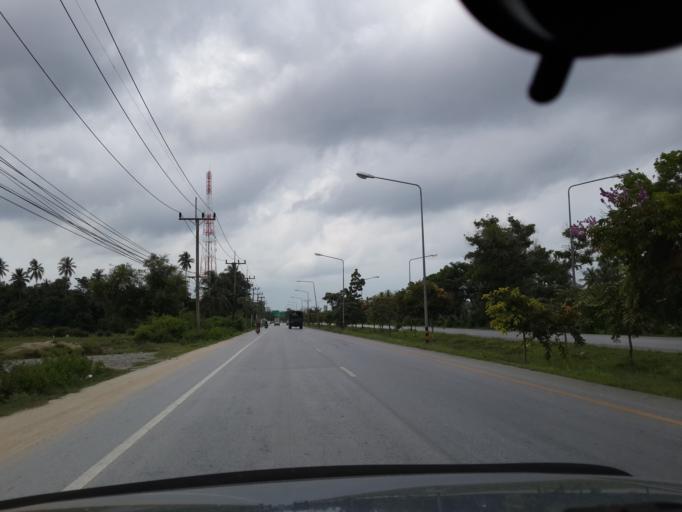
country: TH
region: Pattani
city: Pattani
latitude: 6.8714
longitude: 101.2882
